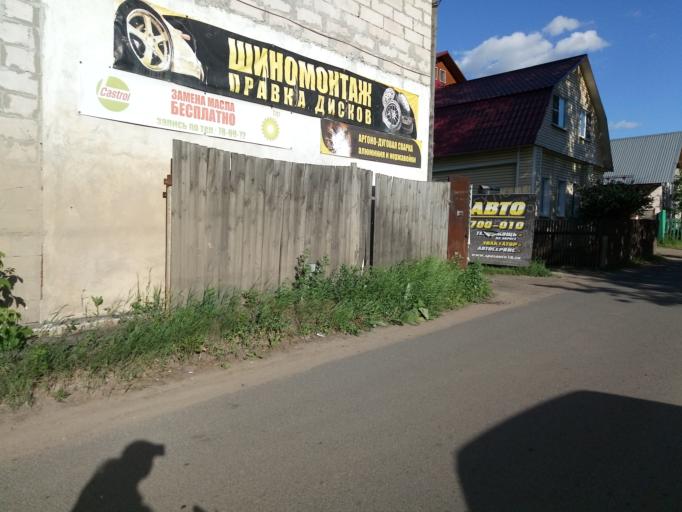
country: RU
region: Jaroslavl
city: Yaroslavl
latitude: 57.6407
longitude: 39.9150
